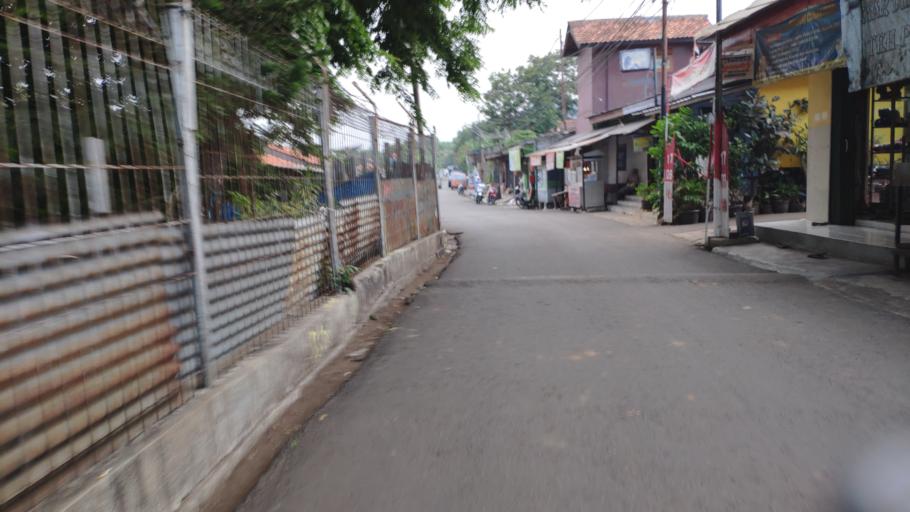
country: ID
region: Jakarta Raya
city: Jakarta
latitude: -6.2953
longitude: 106.8116
